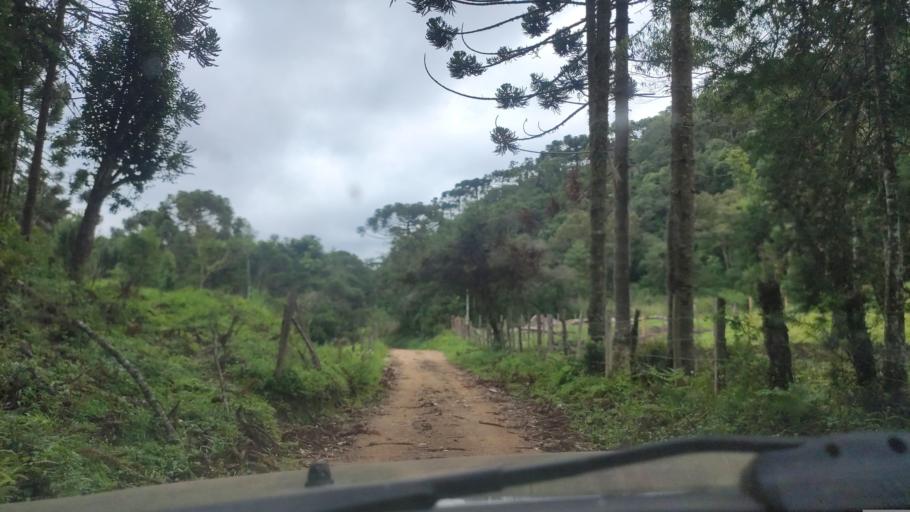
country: BR
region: Minas Gerais
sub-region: Paraisopolis
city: Paraisopolis
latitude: -22.7181
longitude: -45.8488
